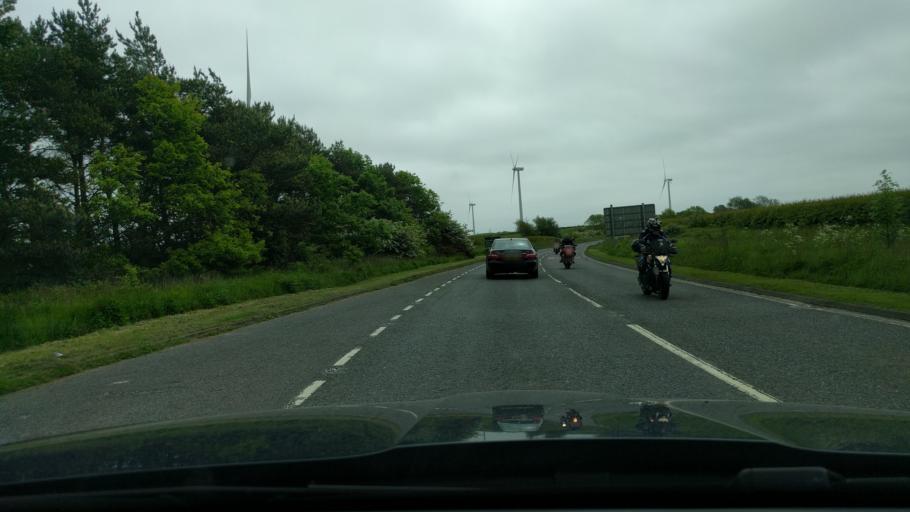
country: GB
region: England
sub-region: Northumberland
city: Cresswell
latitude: 55.2083
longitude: -1.5713
